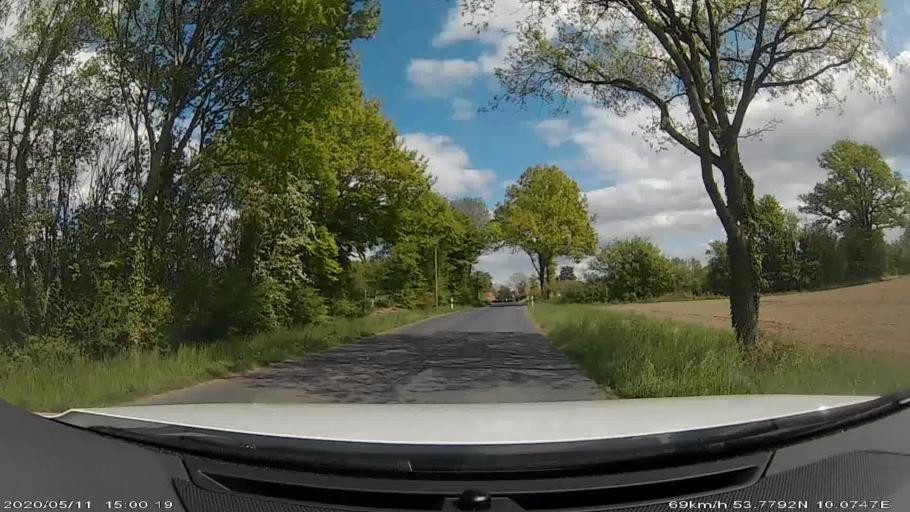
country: DE
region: Schleswig-Holstein
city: Tangstedt
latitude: 53.7831
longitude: 10.0811
